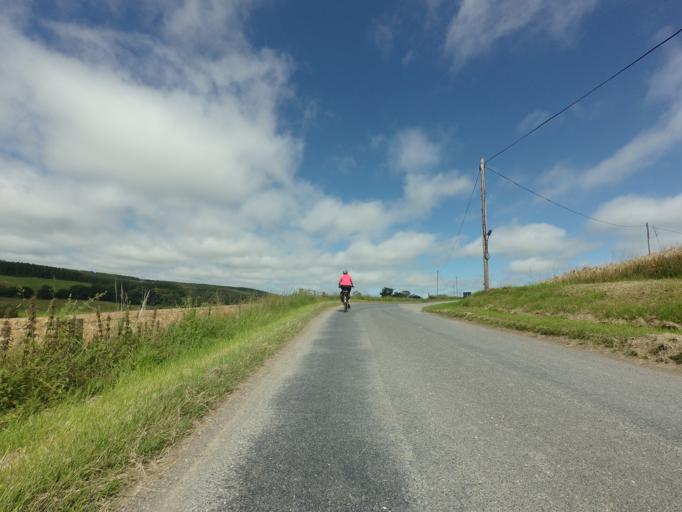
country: GB
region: Scotland
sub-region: Aberdeenshire
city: Turriff
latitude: 57.5671
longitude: -2.4956
